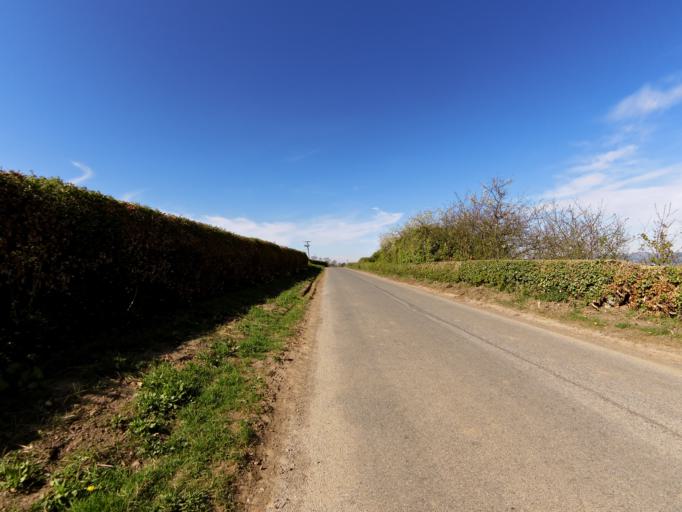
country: GB
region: Scotland
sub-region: Dundee City
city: Dundee
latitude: 56.4078
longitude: -3.0405
